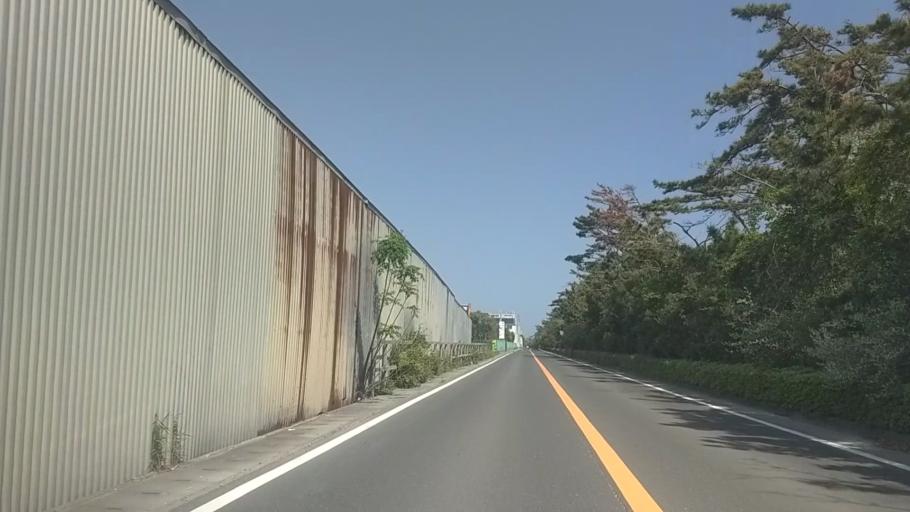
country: JP
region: Shizuoka
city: Hamamatsu
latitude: 34.6713
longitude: 137.6848
